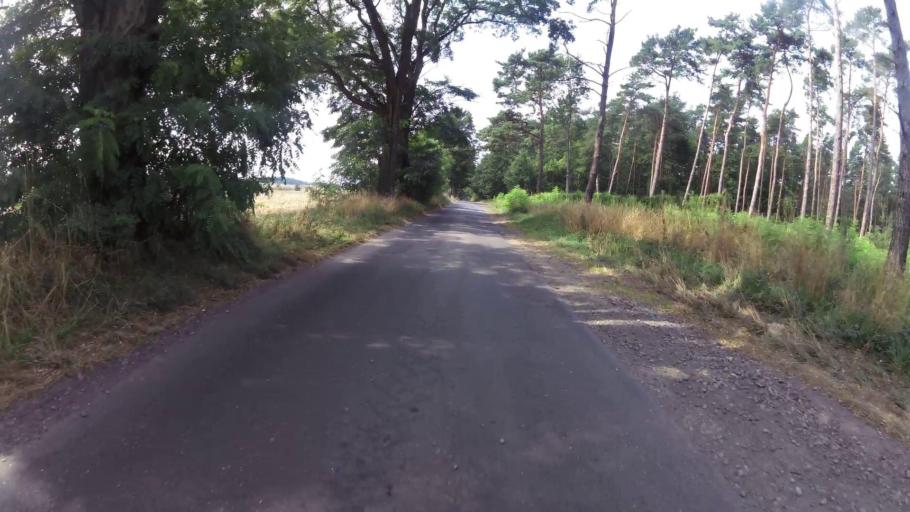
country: PL
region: West Pomeranian Voivodeship
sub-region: Powiat gryfinski
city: Mieszkowice
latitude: 52.8720
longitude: 14.5174
